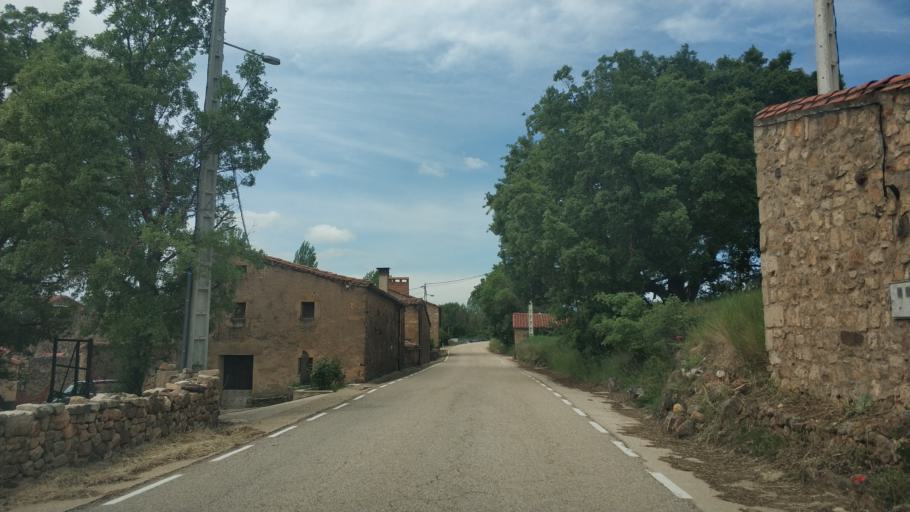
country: ES
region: Castille and Leon
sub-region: Provincia de Soria
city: Sotillo del Rincon
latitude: 41.8858
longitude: -2.6161
